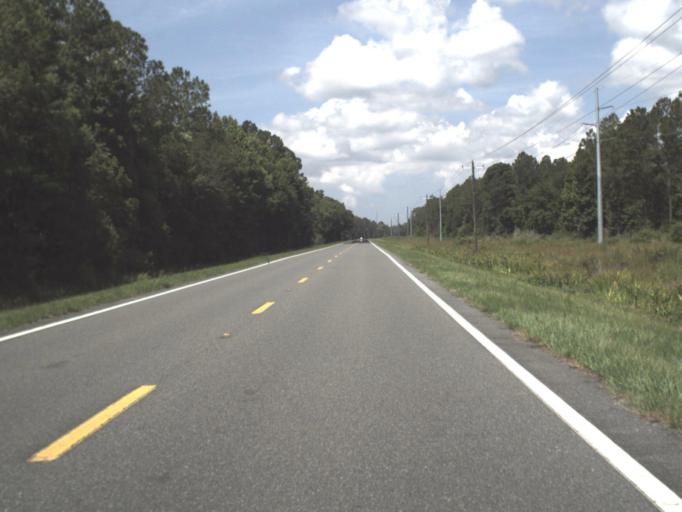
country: US
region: Florida
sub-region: Levy County
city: Chiefland
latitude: 29.2551
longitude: -82.8977
